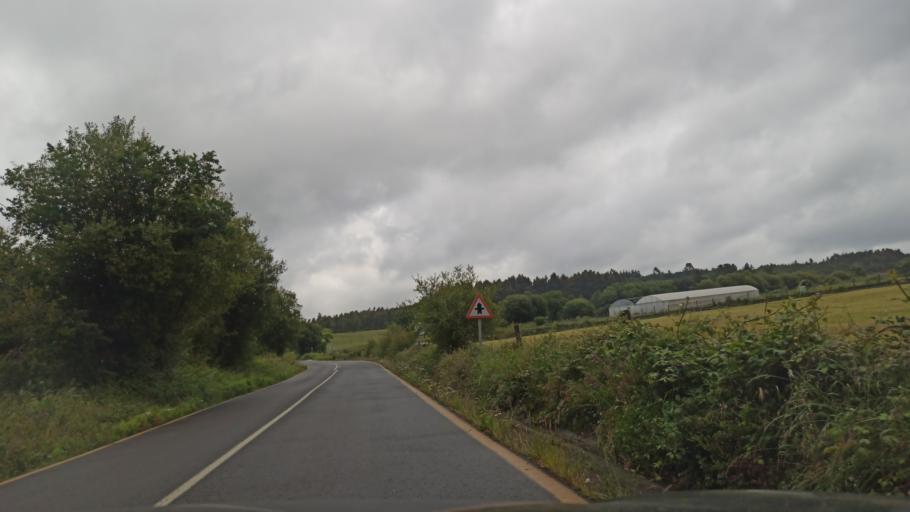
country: ES
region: Galicia
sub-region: Provincia da Coruna
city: Santiso
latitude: 42.7707
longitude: -8.0290
